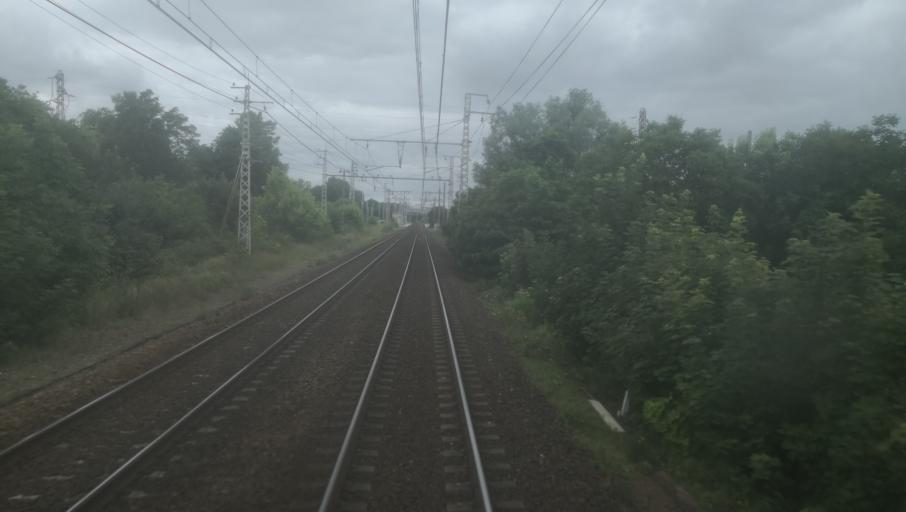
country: FR
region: Midi-Pyrenees
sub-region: Departement de la Haute-Garonne
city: Saint-Jory
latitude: 43.7356
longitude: 1.3738
